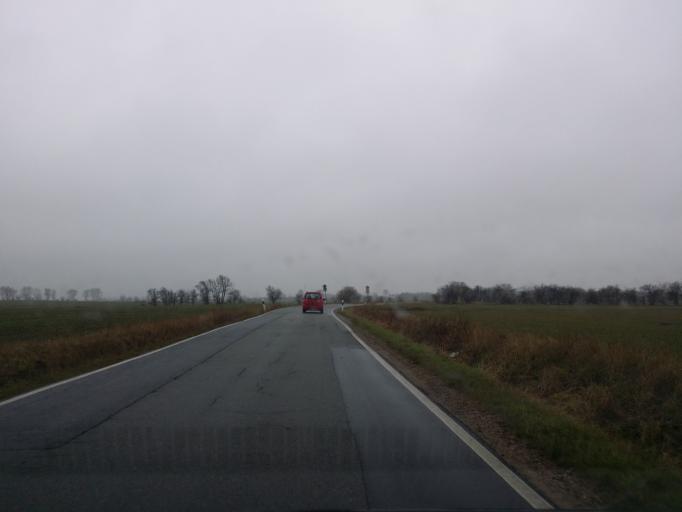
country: DE
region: Schleswig-Holstein
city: Fehmarn
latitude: 54.4303
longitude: 11.1615
